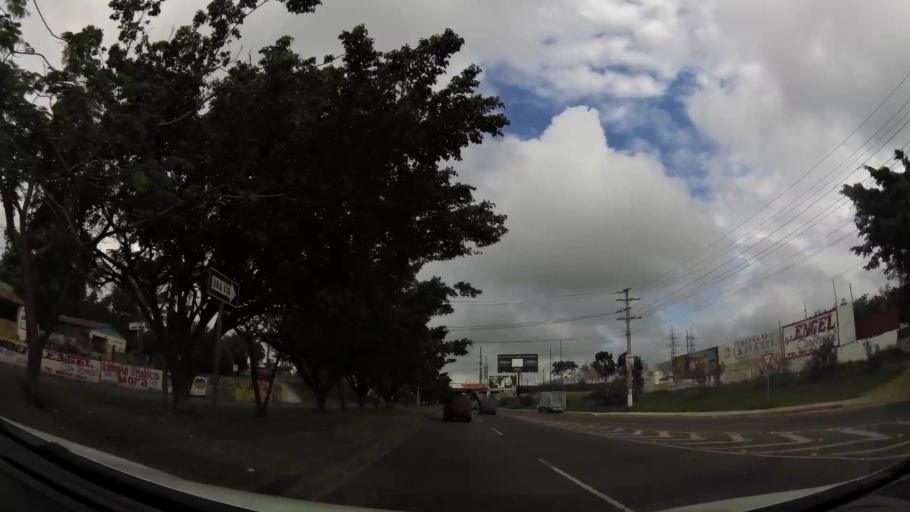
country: DO
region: Santiago
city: Licey al Medio
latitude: 19.4131
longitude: -70.6423
